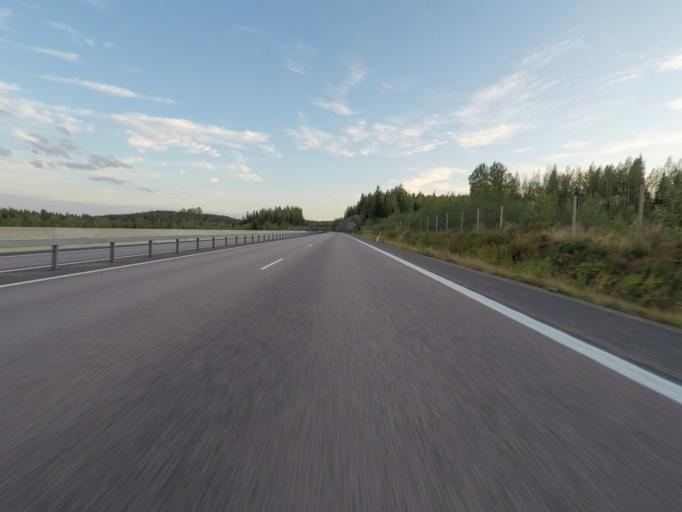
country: FI
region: Central Finland
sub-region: Jyvaeskylae
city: Saeynaetsalo
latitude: 62.2197
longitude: 25.8946
